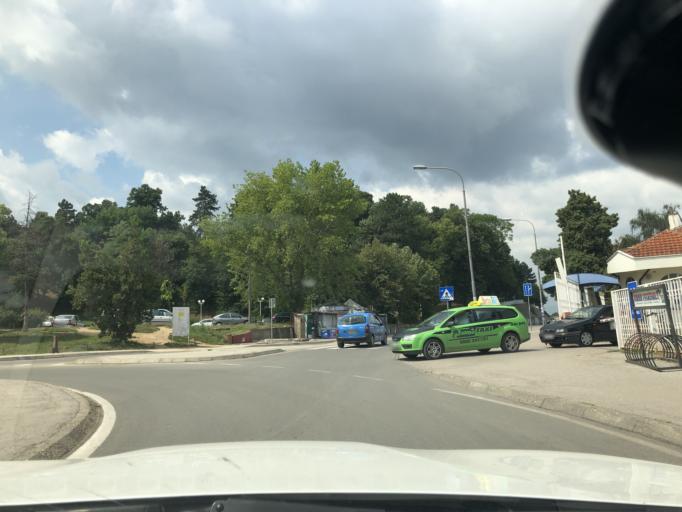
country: RS
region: Central Serbia
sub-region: Jablanicki Okrug
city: Leskovac
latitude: 42.9944
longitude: 21.9386
